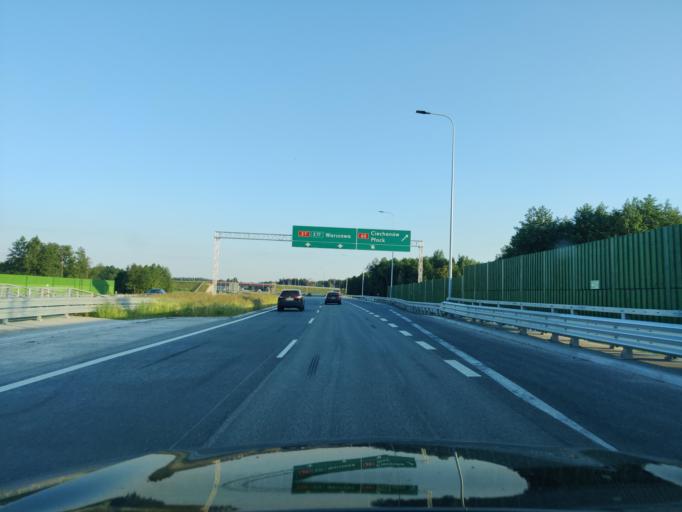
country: PL
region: Masovian Voivodeship
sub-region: Powiat ciechanowski
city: Glinojeck
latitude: 52.8274
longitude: 20.2611
